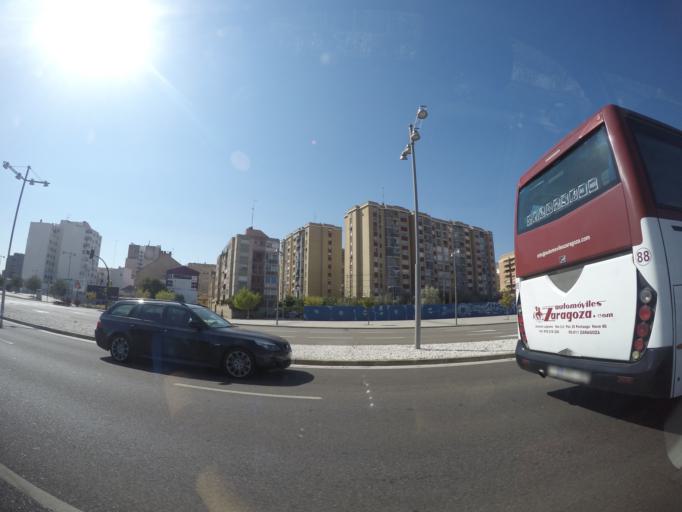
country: ES
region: Aragon
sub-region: Provincia de Zaragoza
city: Almozara
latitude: 41.6570
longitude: -0.9014
